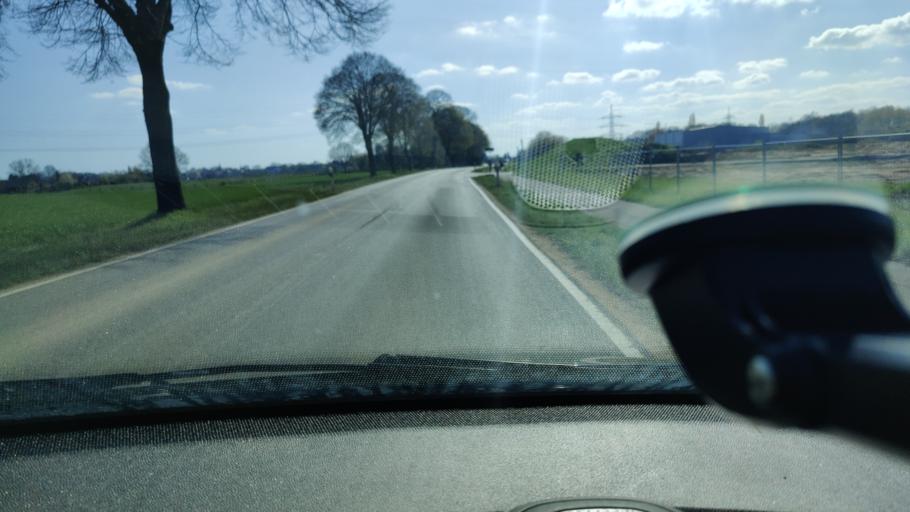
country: DE
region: North Rhine-Westphalia
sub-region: Regierungsbezirk Dusseldorf
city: Wesel
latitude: 51.6204
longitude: 6.6260
